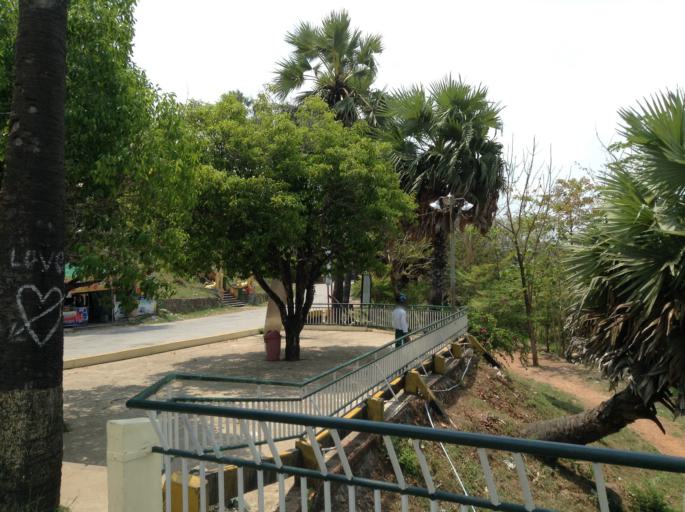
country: MM
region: Mon
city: Mawlamyine
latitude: 16.4803
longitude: 97.6284
